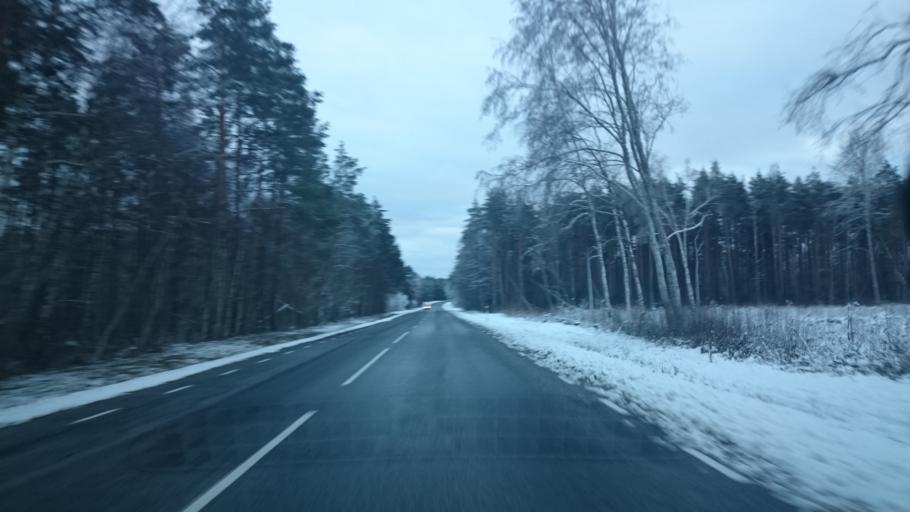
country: EE
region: Saare
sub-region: Kuressaare linn
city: Kuressaare
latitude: 58.3983
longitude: 22.6436
